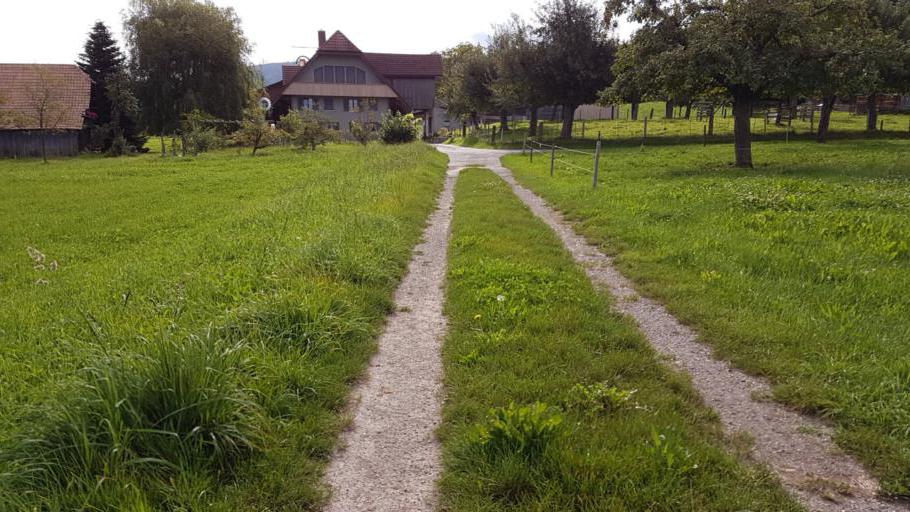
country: CH
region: Bern
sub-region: Bern-Mittelland District
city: Konolfingen
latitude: 46.8729
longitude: 7.6062
